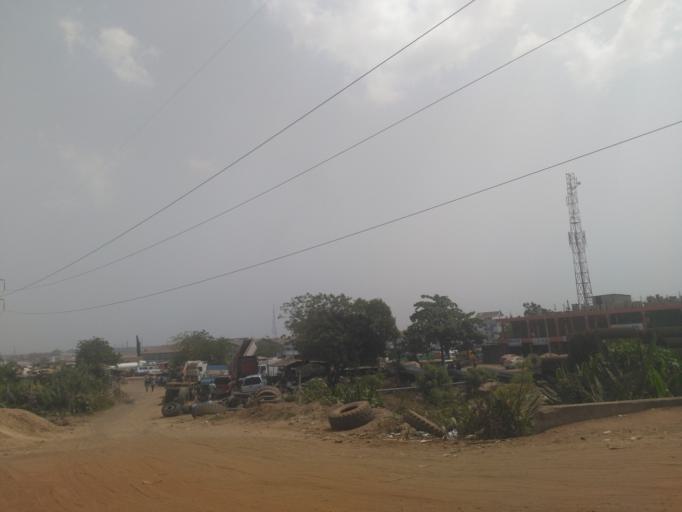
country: GH
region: Greater Accra
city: Tema
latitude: 5.6899
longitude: -0.0136
